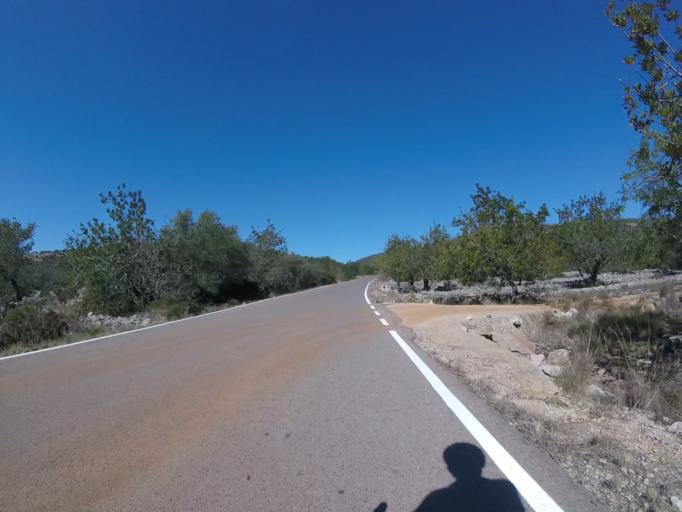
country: ES
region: Valencia
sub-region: Provincia de Castello
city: Santa Magdalena de Pulpis
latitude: 40.3807
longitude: 0.2649
